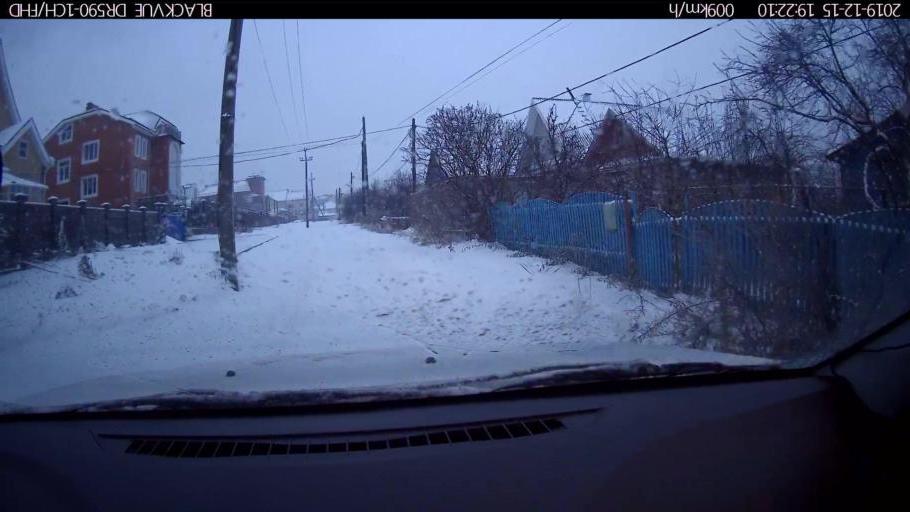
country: RU
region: Nizjnij Novgorod
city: Afonino
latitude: 56.3049
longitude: 44.0875
